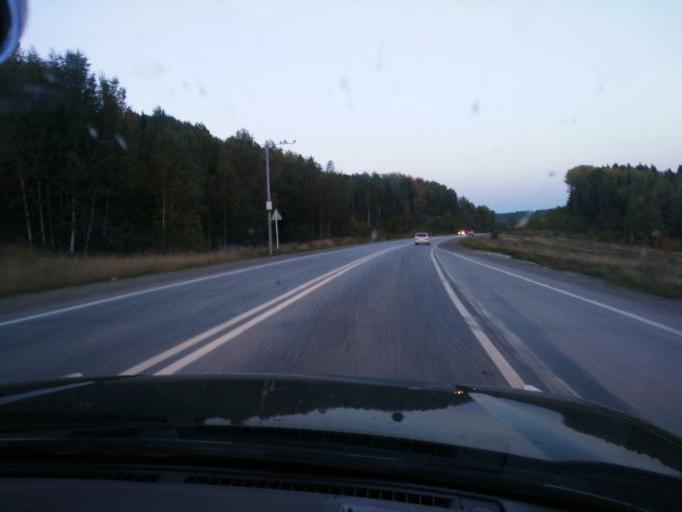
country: RU
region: Perm
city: Verkhnechusovskiye Gorodki
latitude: 58.2961
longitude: 56.8655
